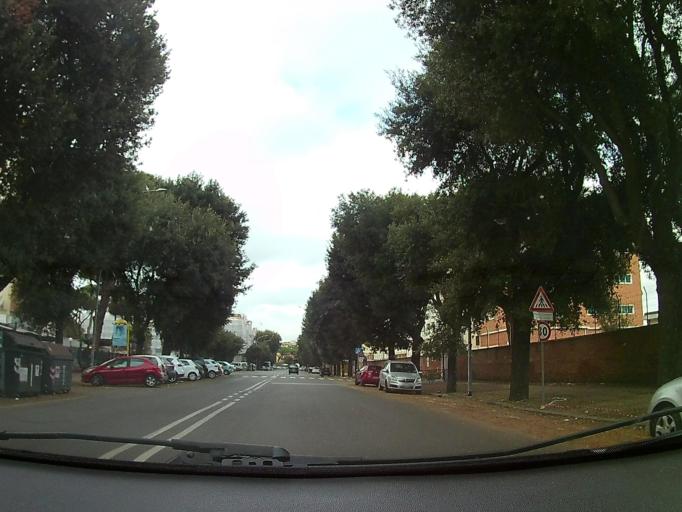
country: IT
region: Latium
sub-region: Citta metropolitana di Roma Capitale
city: Lido di Ostia
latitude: 41.7325
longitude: 12.2934
